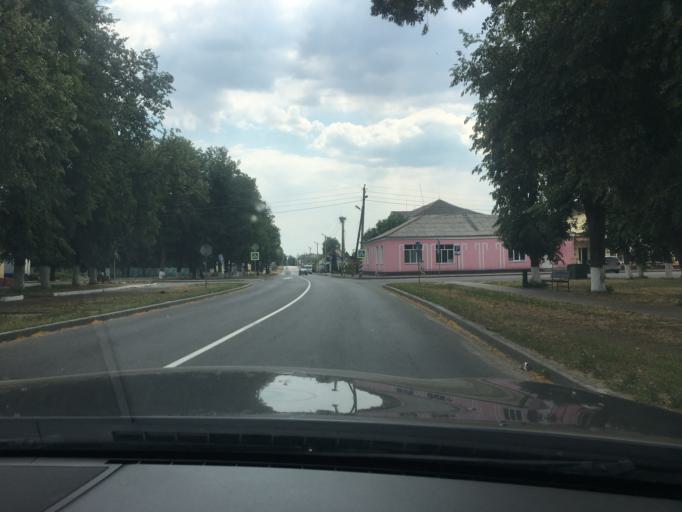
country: BY
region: Brest
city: Ruzhany
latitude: 52.8665
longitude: 24.8906
